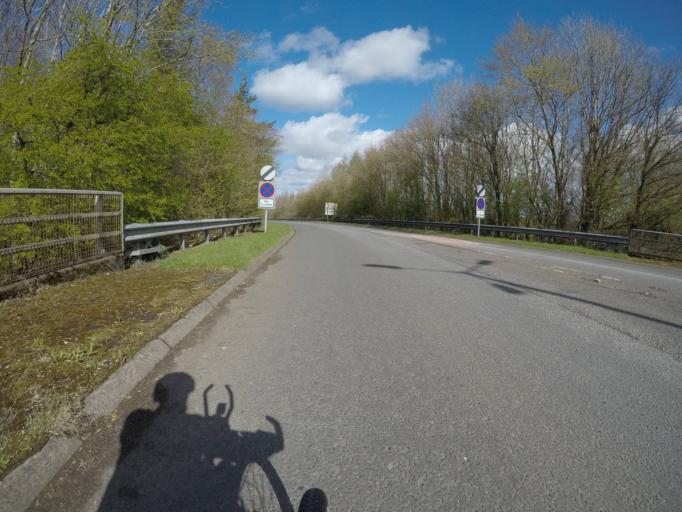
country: GB
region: Scotland
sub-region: North Ayrshire
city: Springside
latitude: 55.6128
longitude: -4.6040
